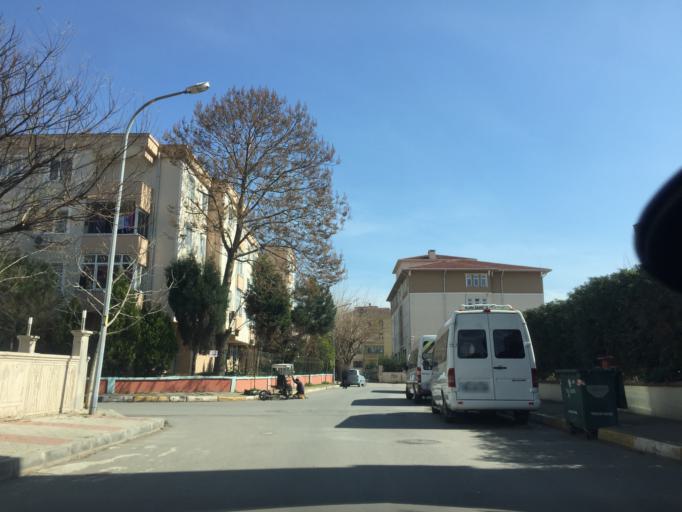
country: TR
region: Istanbul
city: Icmeler
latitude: 40.8284
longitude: 29.3187
